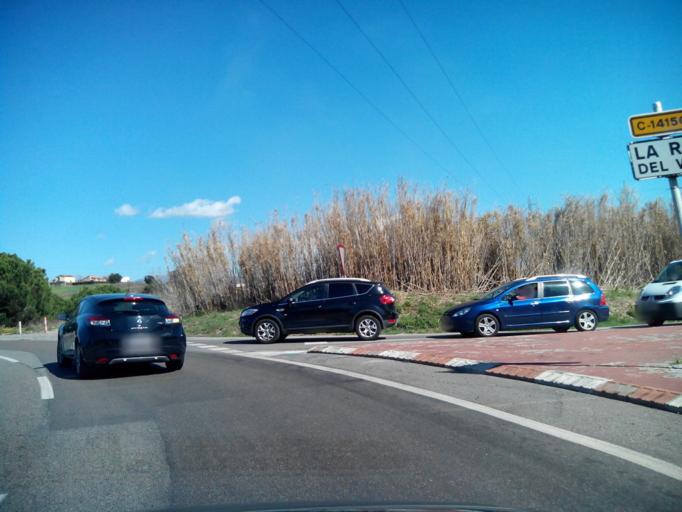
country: ES
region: Catalonia
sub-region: Provincia de Barcelona
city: La Roca del Valles
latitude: 41.5935
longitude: 2.3157
